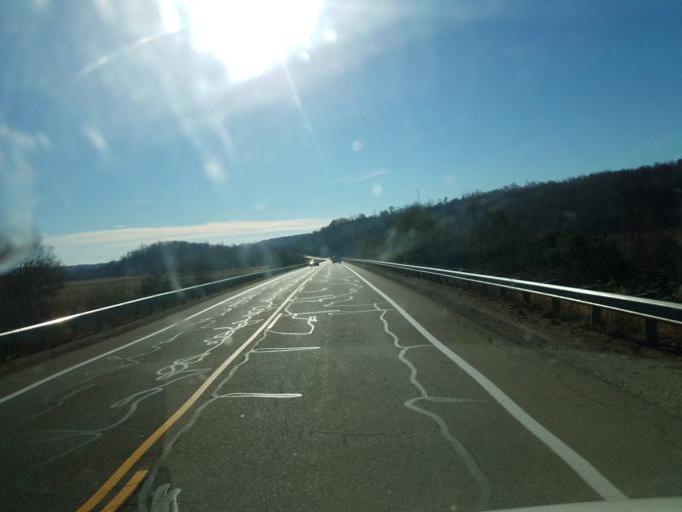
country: US
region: Ohio
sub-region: Muskingum County
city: Dresden
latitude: 40.1397
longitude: -82.0288
